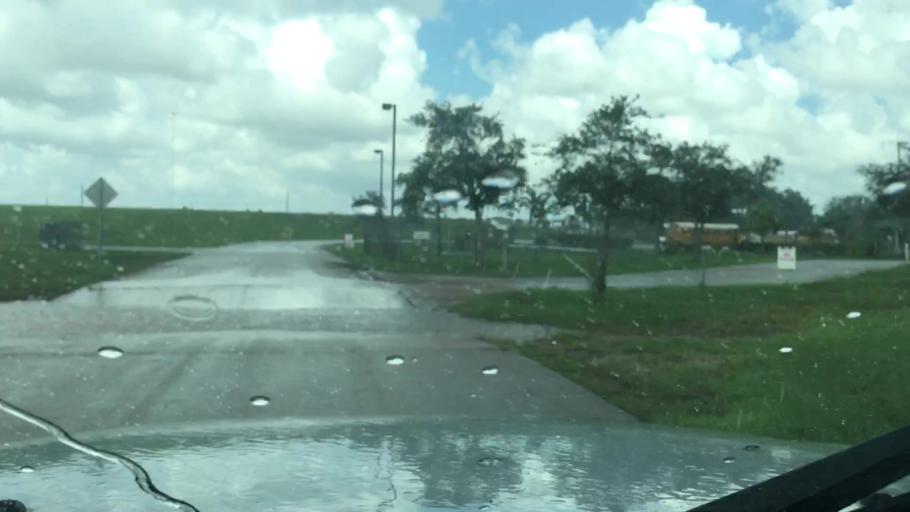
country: US
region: Florida
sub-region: Miami-Dade County
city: Ives Estates
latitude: 25.9706
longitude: -80.1685
